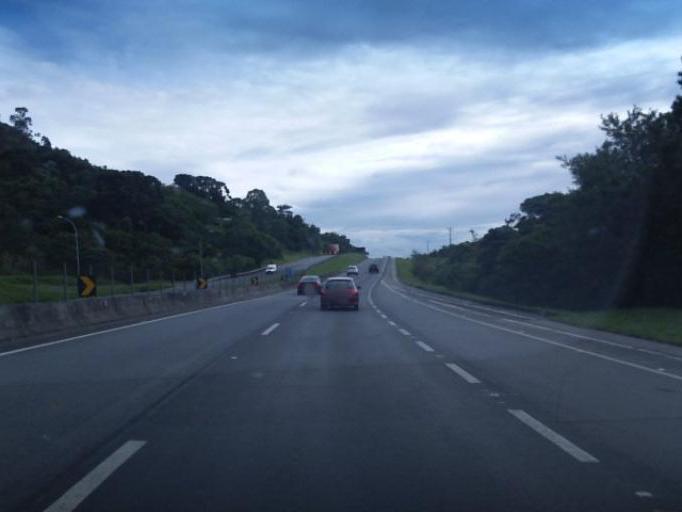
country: BR
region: Parana
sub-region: Campina Grande Do Sul
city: Campina Grande do Sul
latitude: -25.1411
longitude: -48.8563
